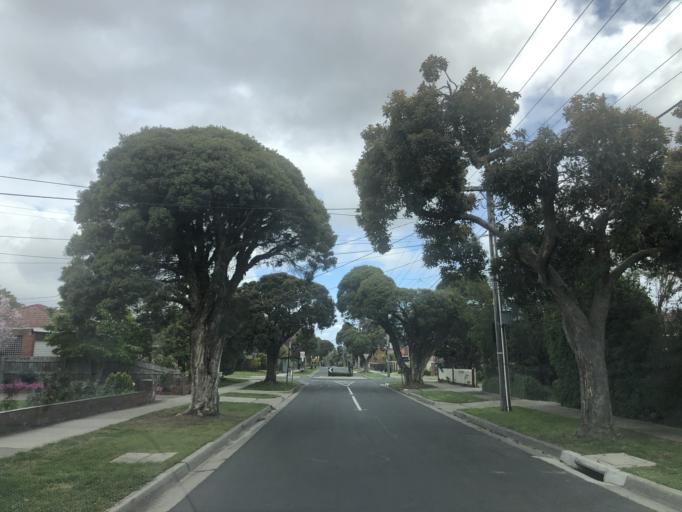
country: AU
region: Victoria
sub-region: Monash
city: Ashwood
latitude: -37.8796
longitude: 145.1245
